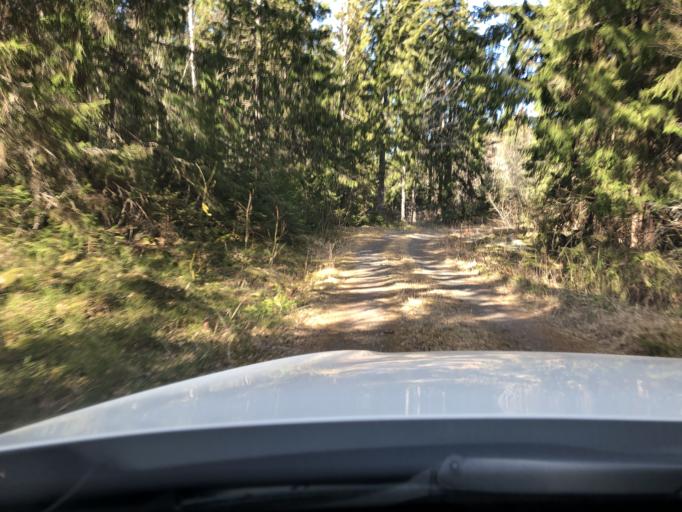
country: SE
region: Uppsala
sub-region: Heby Kommun
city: OEstervala
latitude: 60.3313
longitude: 17.1766
